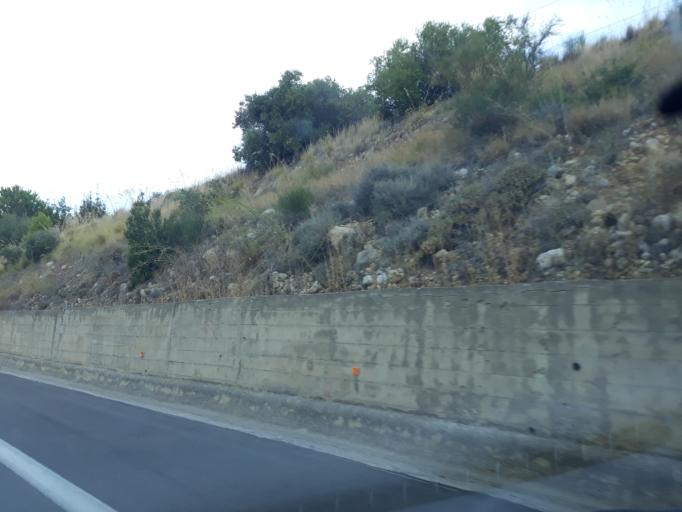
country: IT
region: Sicily
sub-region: Palermo
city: Termini Imerese
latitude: 37.9813
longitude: 13.6685
